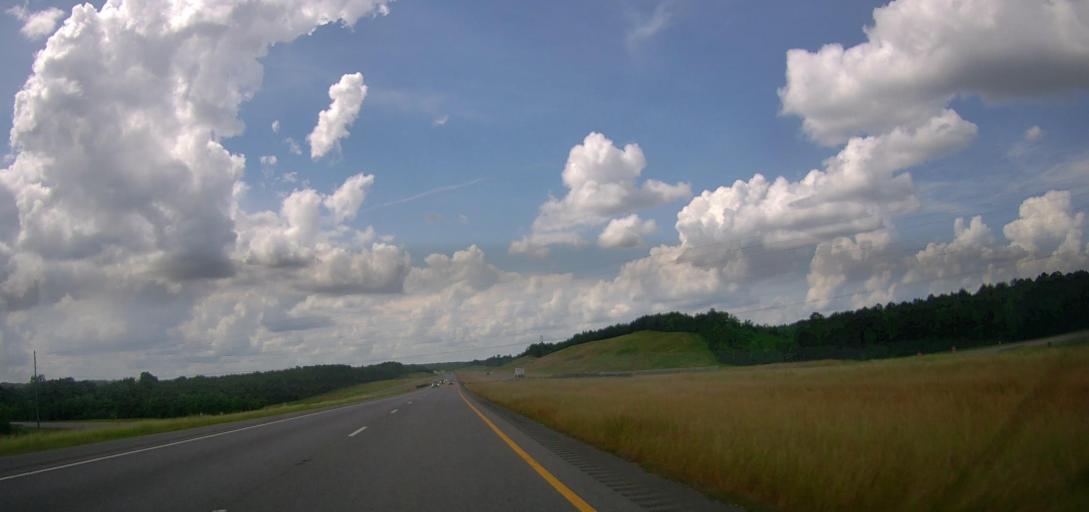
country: US
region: Alabama
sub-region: Walker County
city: Jasper
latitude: 33.8175
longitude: -87.3121
